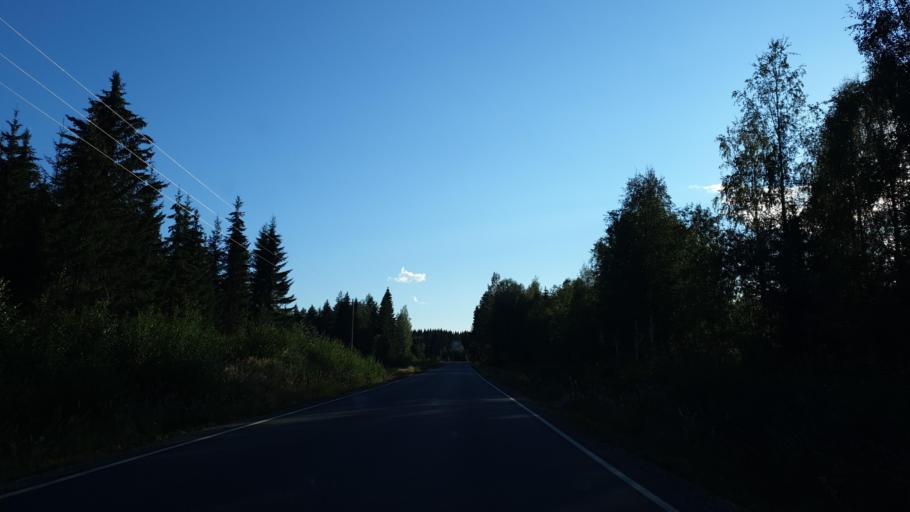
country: FI
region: Northern Savo
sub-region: Koillis-Savo
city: Juankoski
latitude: 63.1806
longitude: 28.3957
